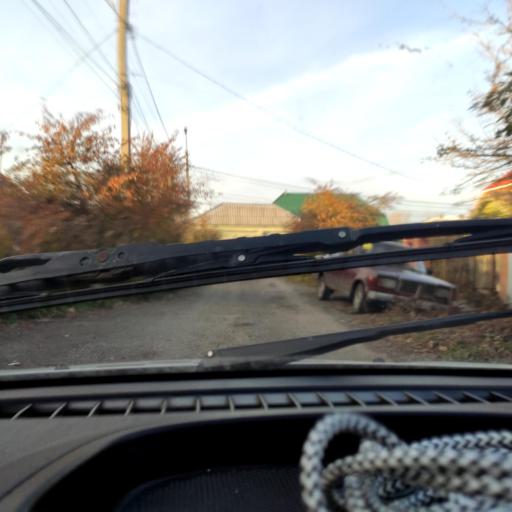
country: RU
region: Samara
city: Tol'yatti
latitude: 53.5318
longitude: 49.4091
